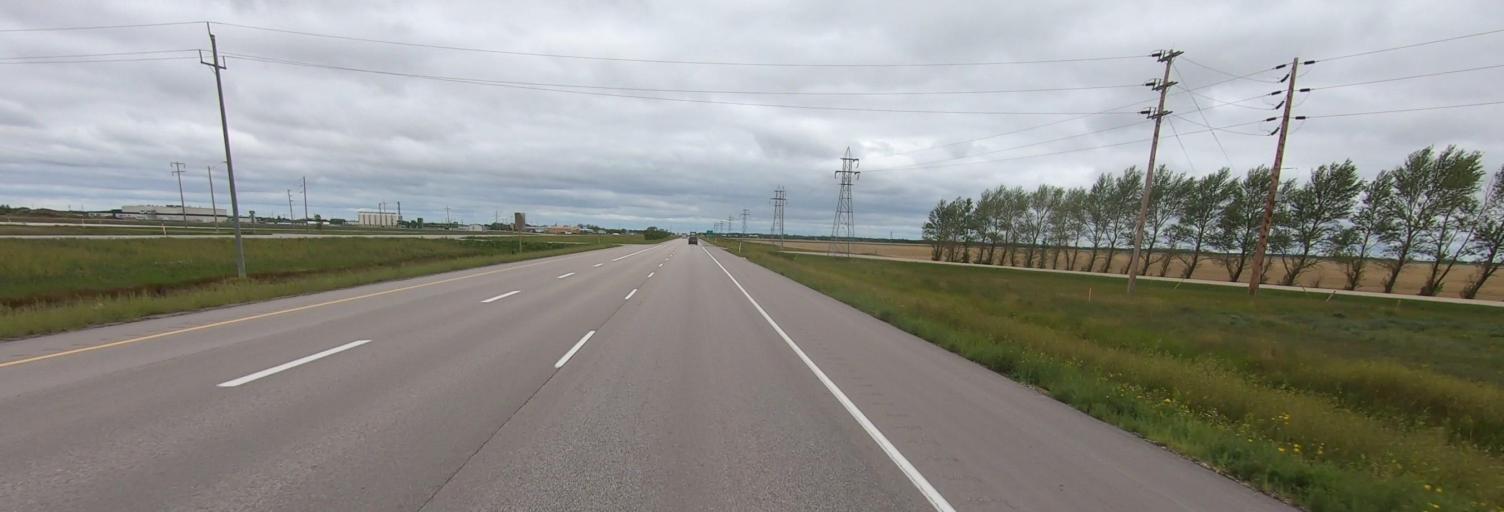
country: CA
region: Manitoba
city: Headingley
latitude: 49.9014
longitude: -97.7231
